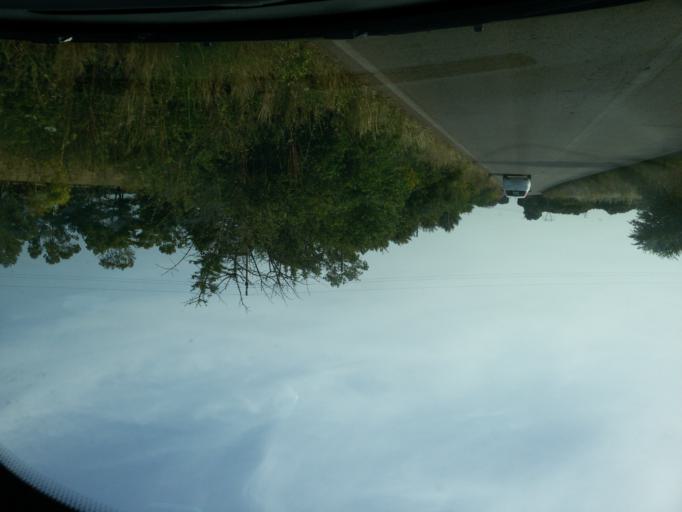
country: IT
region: Apulia
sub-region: Provincia di Brindisi
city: San Pancrazio Salentino
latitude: 40.3367
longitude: 17.8501
